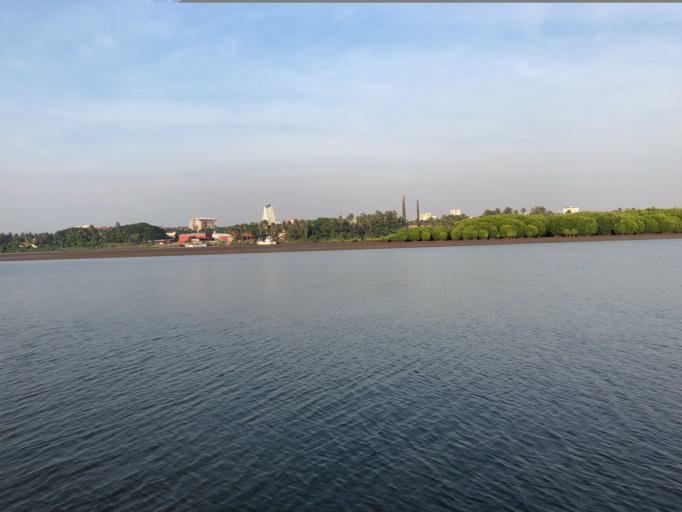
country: IN
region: Karnataka
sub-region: Dakshina Kannada
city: Mangalore
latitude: 12.8777
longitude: 74.8222
